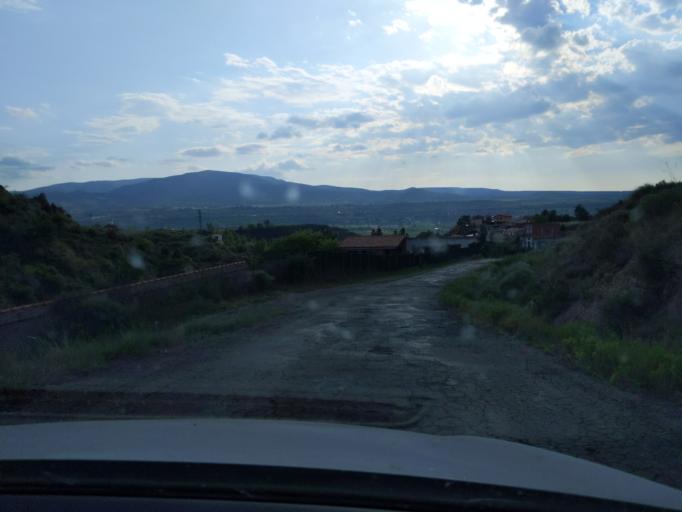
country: ES
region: La Rioja
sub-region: Provincia de La Rioja
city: Albelda de Iregua
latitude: 42.3551
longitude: -2.4658
